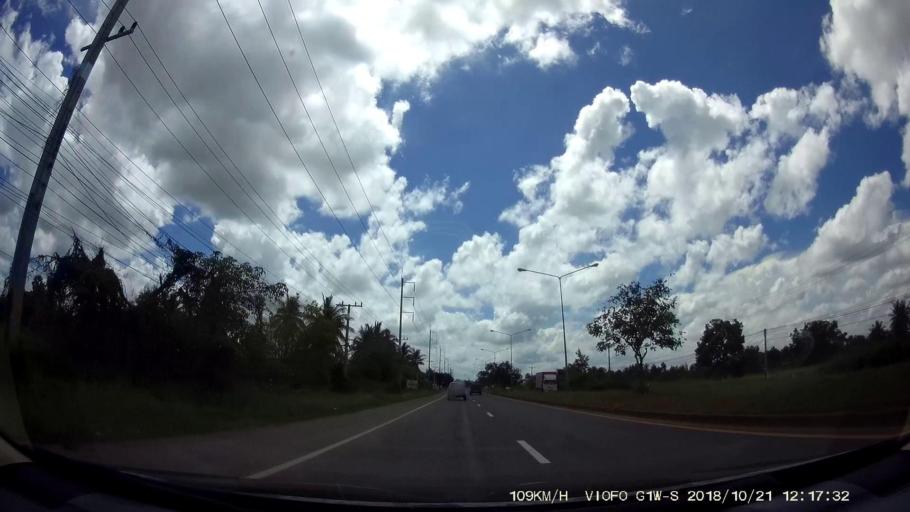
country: TH
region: Nakhon Ratchasima
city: Dan Khun Thot
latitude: 15.3305
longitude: 101.8199
